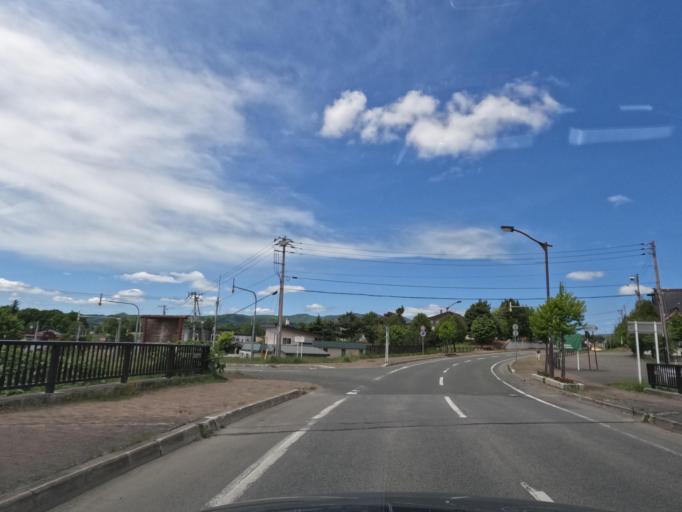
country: JP
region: Hokkaido
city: Shimo-furano
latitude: 43.4607
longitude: 142.4626
